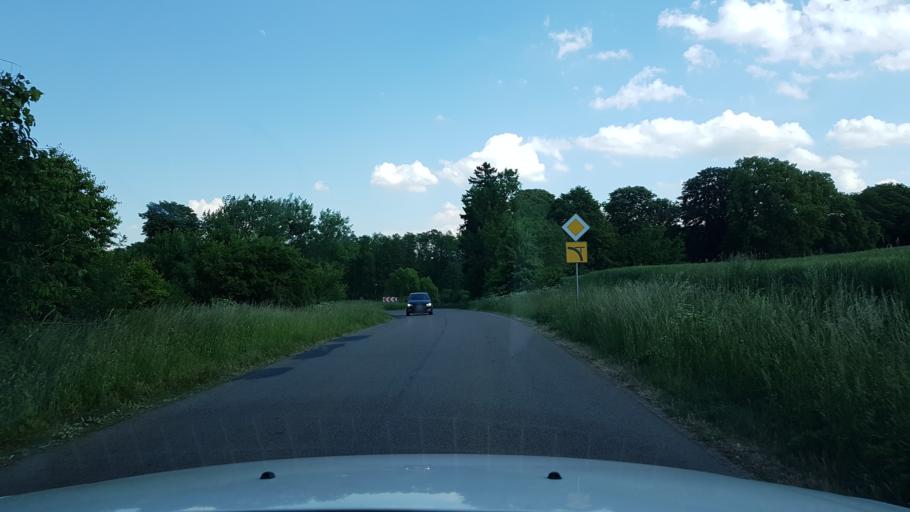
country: PL
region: West Pomeranian Voivodeship
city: Trzcinsko Zdroj
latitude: 53.0334
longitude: 14.6196
